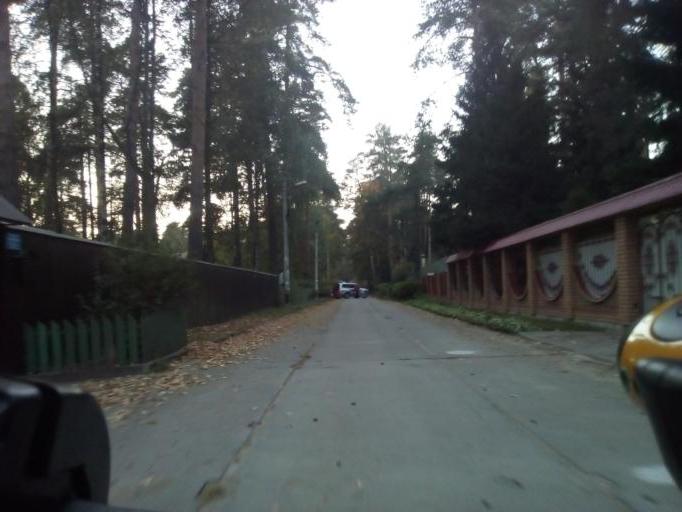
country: RU
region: Moskovskaya
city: Kratovo
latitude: 55.5983
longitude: 38.1828
